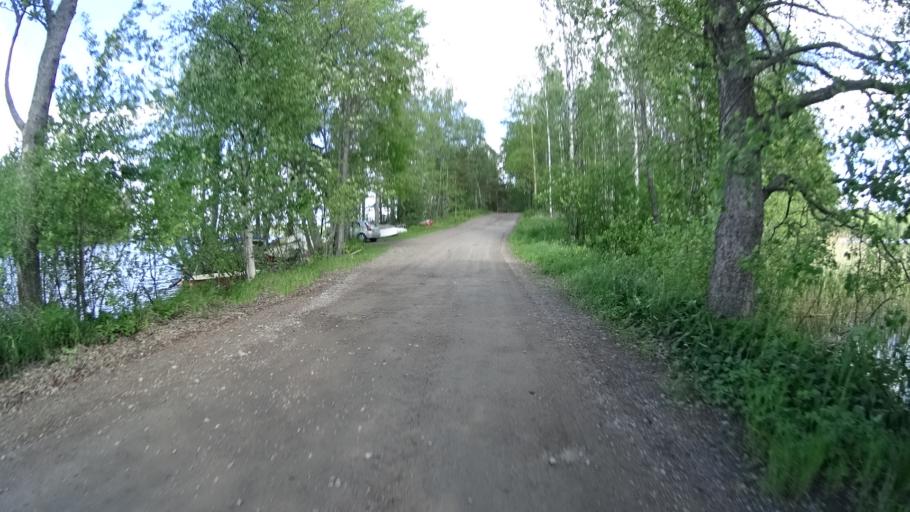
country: FI
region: Uusimaa
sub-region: Raaseporin
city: Pohja
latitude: 60.1250
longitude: 23.6018
